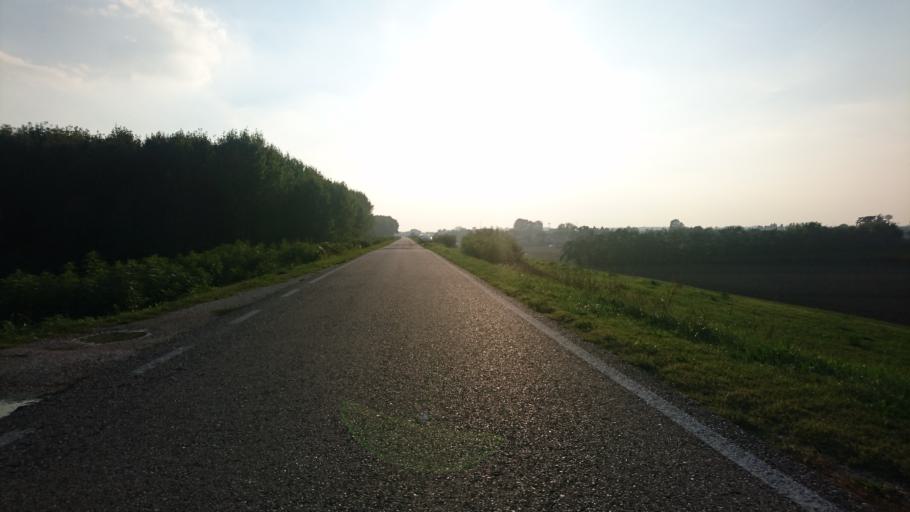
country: IT
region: Emilia-Romagna
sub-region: Provincia di Ferrara
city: Francolino
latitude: 44.8964
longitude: 11.6324
